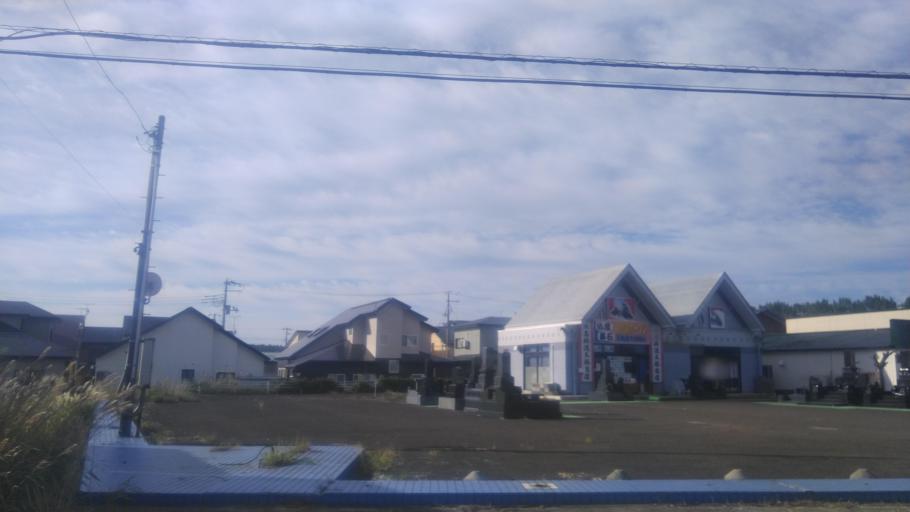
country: JP
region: Akita
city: Noshiromachi
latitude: 40.1851
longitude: 140.0503
